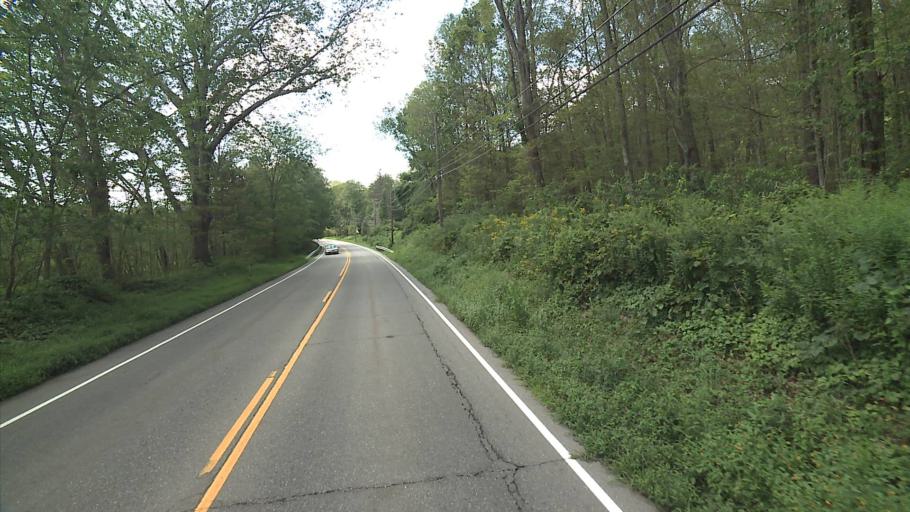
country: US
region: Connecticut
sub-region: Windham County
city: Windham
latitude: 41.8075
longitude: -72.1197
